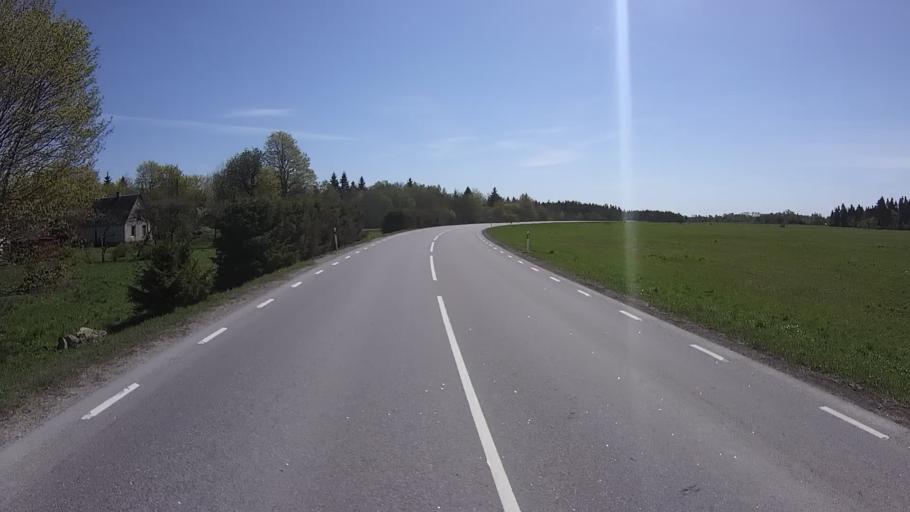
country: EE
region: Harju
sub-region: Keila linn
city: Keila
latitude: 59.3052
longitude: 24.3244
